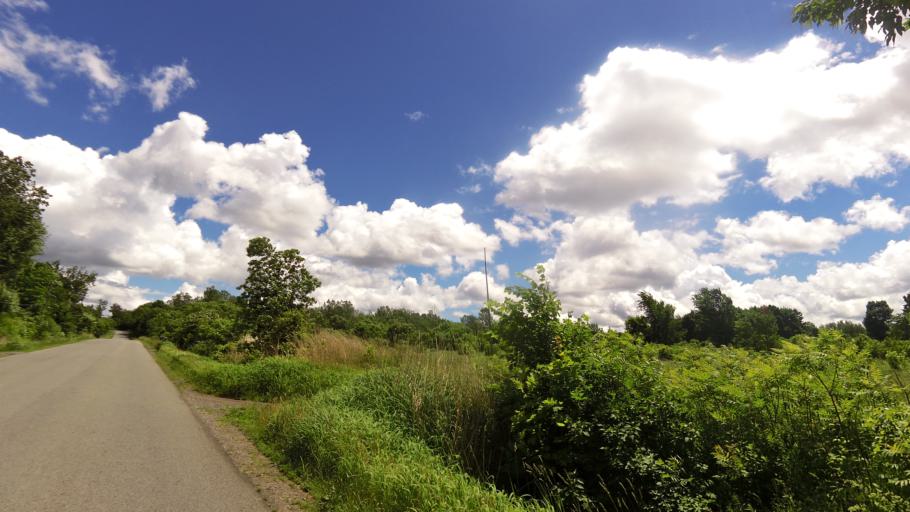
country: CA
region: Quebec
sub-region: Monteregie
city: Hudson
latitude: 45.4815
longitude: -74.1270
